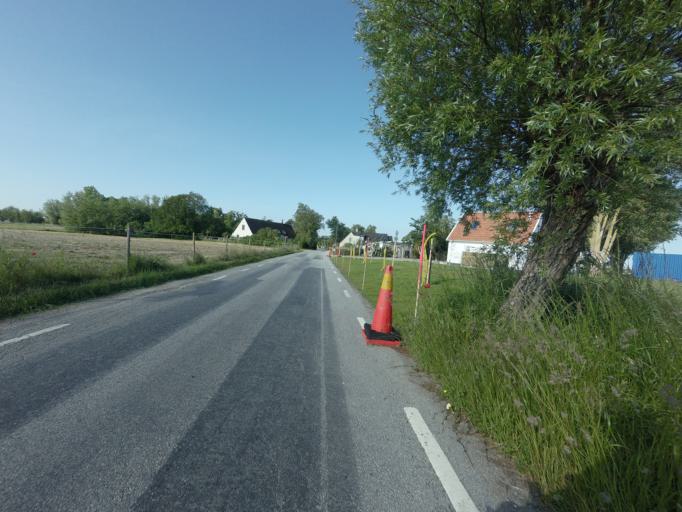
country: SE
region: Skane
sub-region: Trelleborgs Kommun
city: Skare
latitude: 55.4154
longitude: 13.0117
